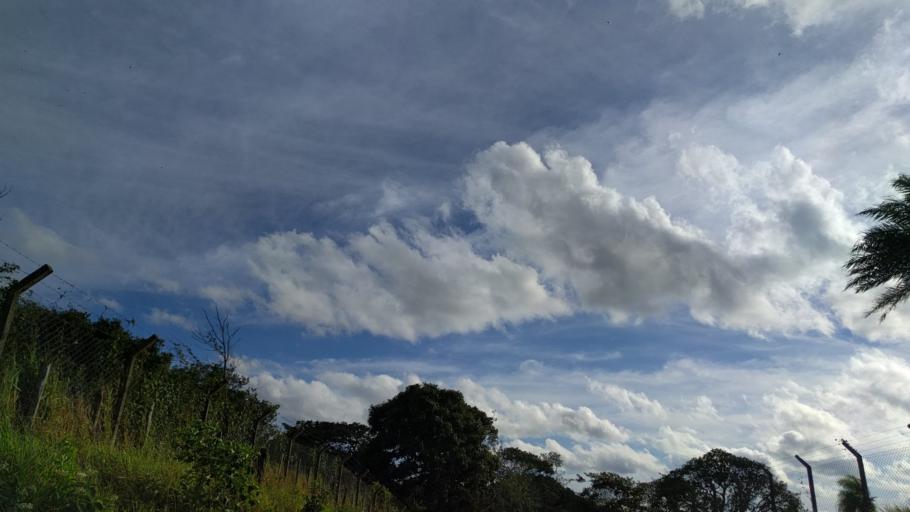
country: BO
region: Santa Cruz
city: Santa Cruz de la Sierra
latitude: -17.8547
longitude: -63.2655
